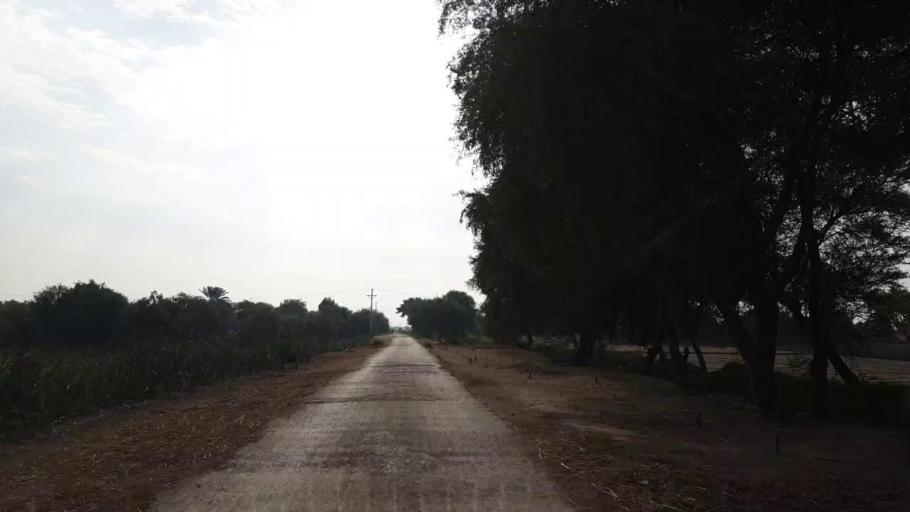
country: PK
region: Sindh
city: Tando Muhammad Khan
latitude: 25.0353
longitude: 68.4369
